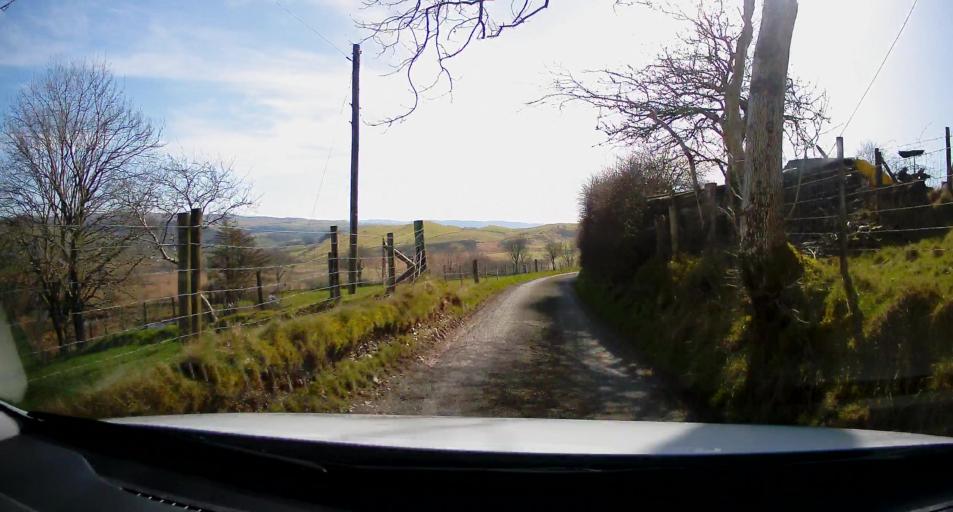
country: GB
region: Wales
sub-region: County of Ceredigion
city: Lledrod
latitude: 52.3652
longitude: -3.8666
